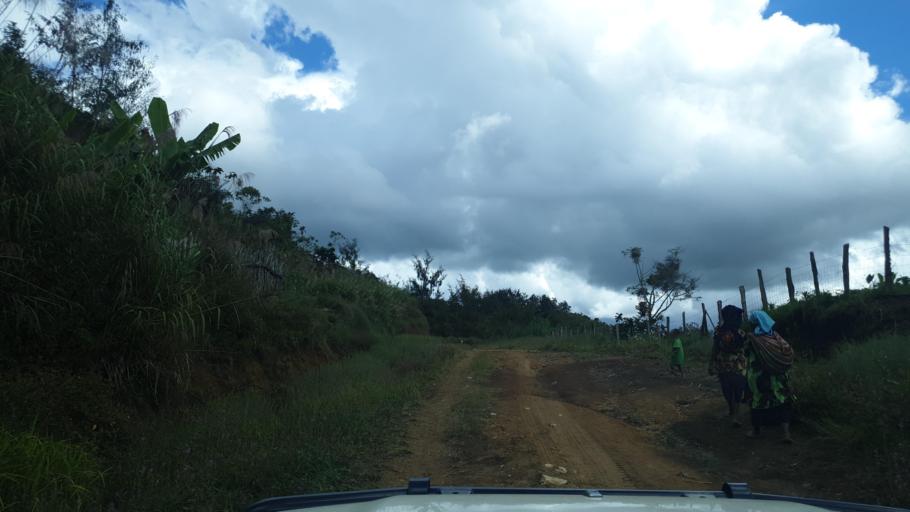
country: PG
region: Eastern Highlands
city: Goroka
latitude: -6.2756
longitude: 145.1892
